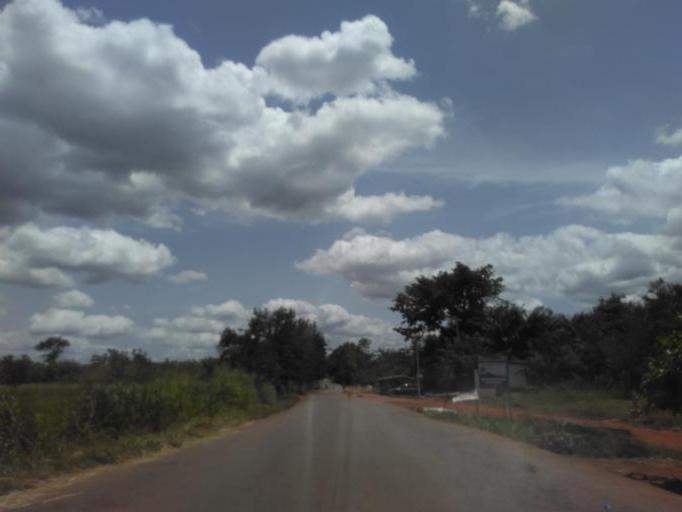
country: GH
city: Akropong
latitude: 6.1097
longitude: -0.1118
